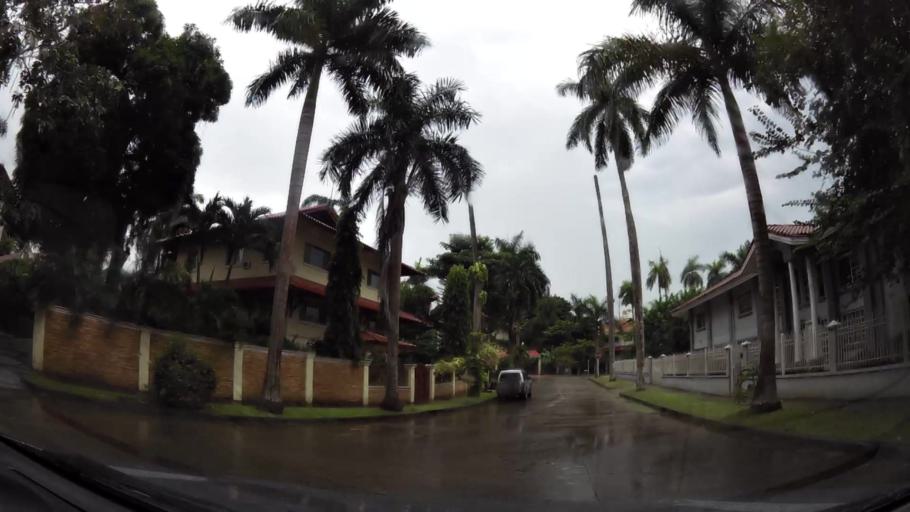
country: PA
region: Panama
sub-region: Distrito de Panama
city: Ancon
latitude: 8.9775
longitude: -79.5601
